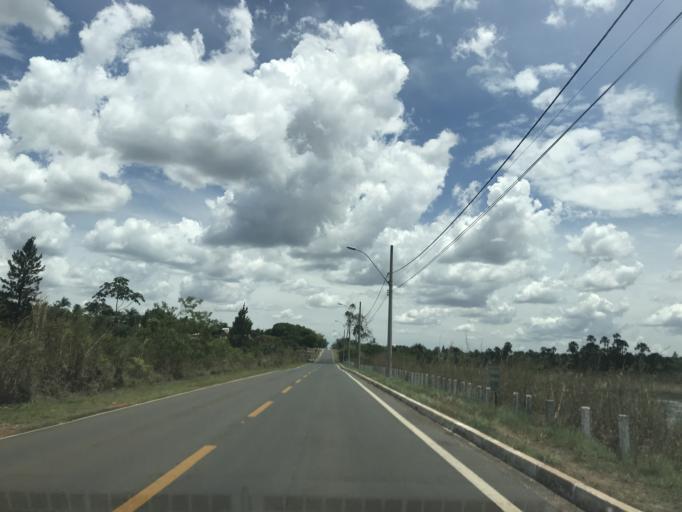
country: BR
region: Federal District
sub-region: Brasilia
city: Brasilia
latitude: -15.8977
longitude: -47.9438
